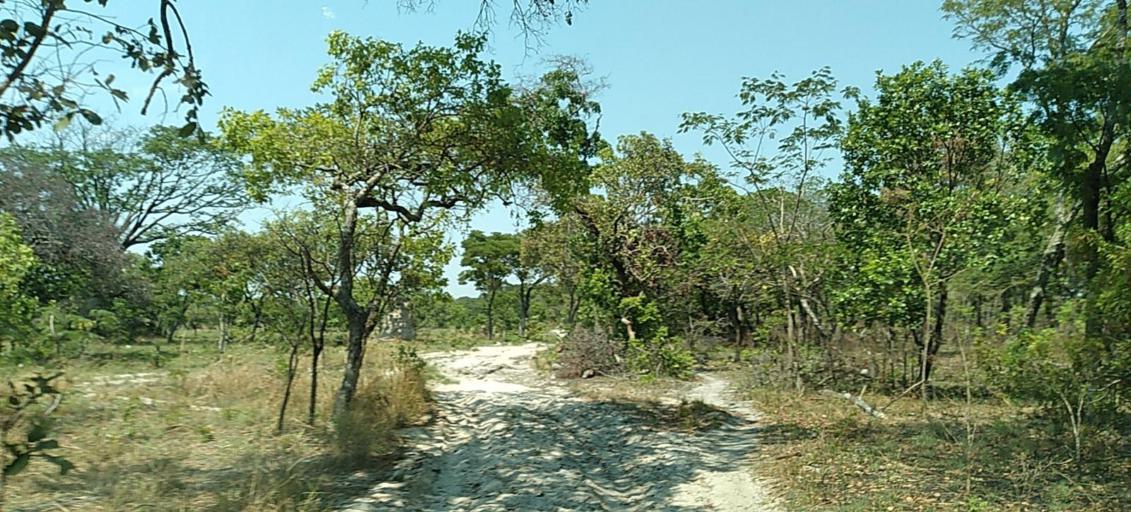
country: ZM
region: Copperbelt
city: Mpongwe
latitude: -13.7796
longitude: 28.1069
